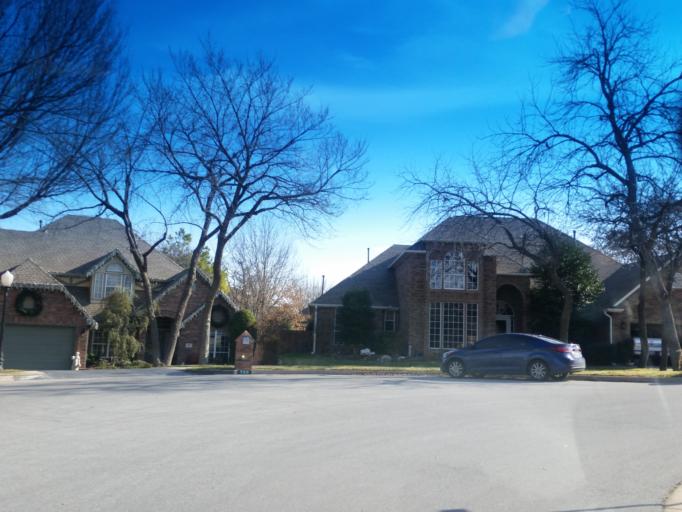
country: US
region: Oklahoma
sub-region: Oklahoma County
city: Edmond
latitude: 35.6474
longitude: -97.4313
